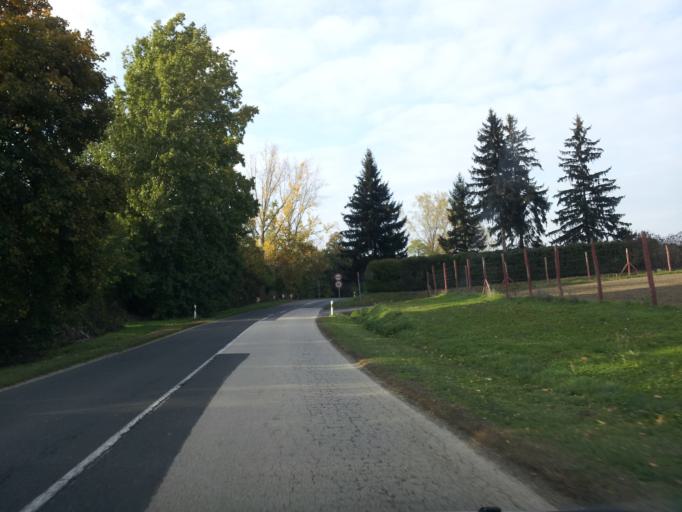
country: HU
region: Gyor-Moson-Sopron
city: Pannonhalma
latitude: 47.5264
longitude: 17.7456
